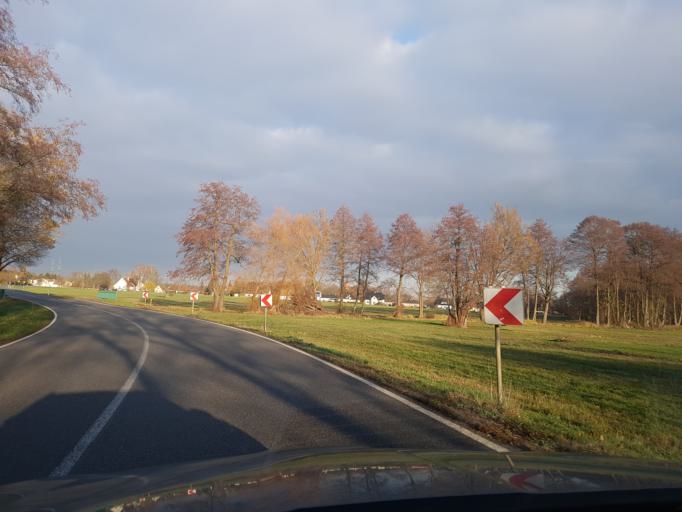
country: DE
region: Brandenburg
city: Luckau
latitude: 51.8740
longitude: 13.6978
